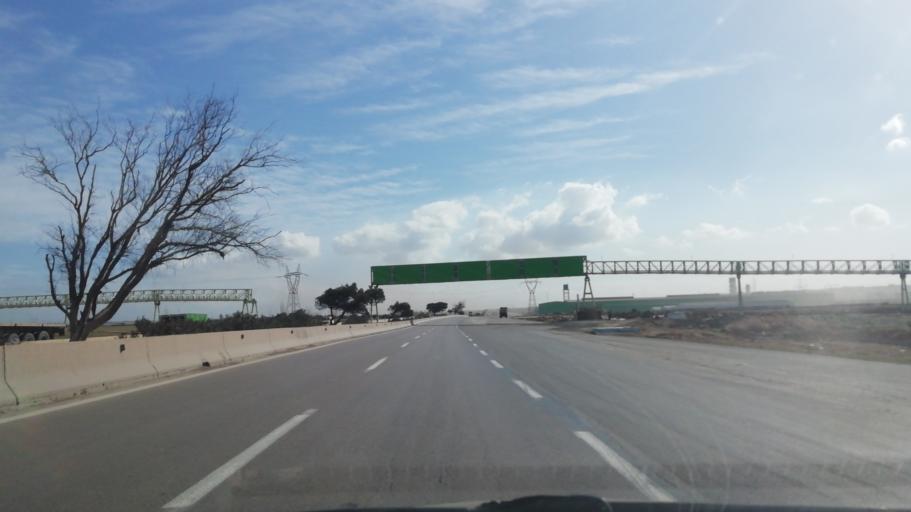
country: DZ
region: Oran
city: Ain el Bya
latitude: 35.7788
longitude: -0.2663
